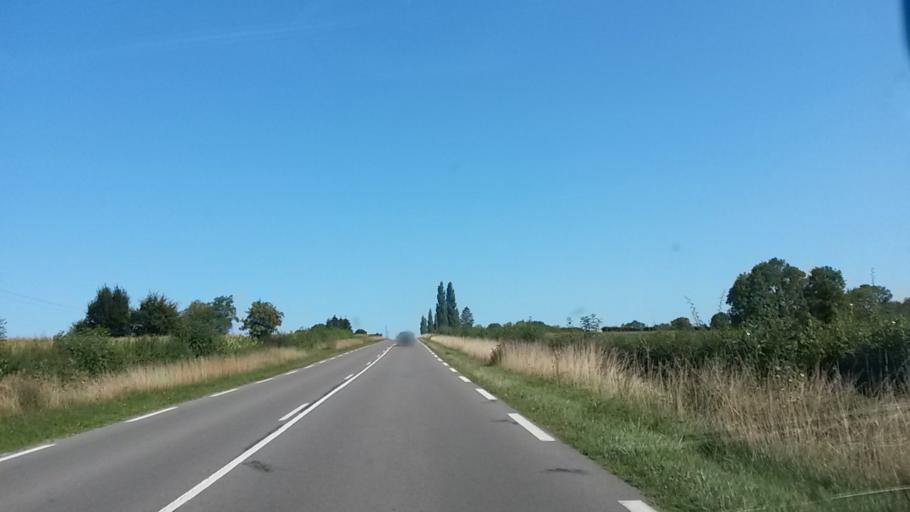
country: FR
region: Nord-Pas-de-Calais
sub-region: Departement du Nord
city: Avesnes-sur-Helpe
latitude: 50.0813
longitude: 3.9296
